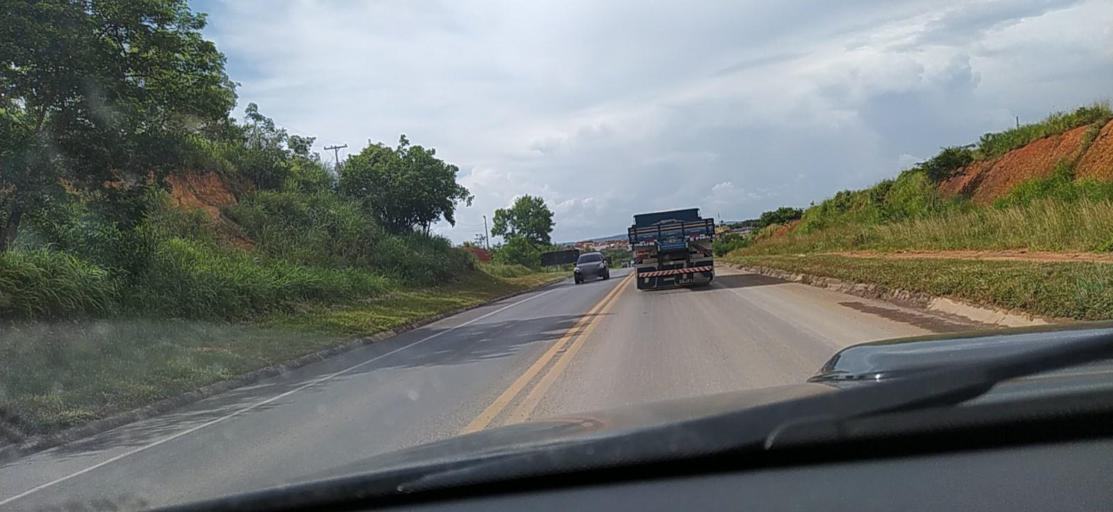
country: BR
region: Minas Gerais
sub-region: Montes Claros
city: Montes Claros
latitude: -16.7562
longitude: -43.8446
